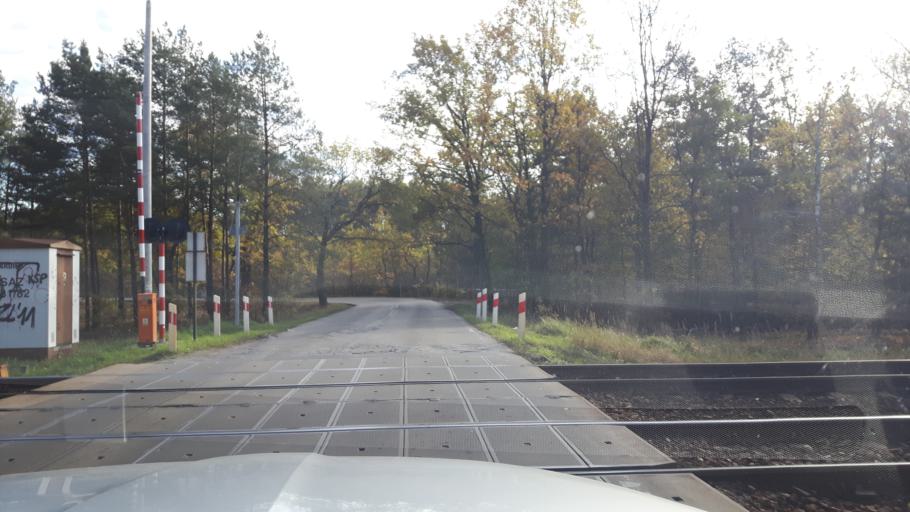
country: PL
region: Masovian Voivodeship
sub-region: Powiat wolominski
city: Zabki
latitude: 52.3000
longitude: 21.1306
